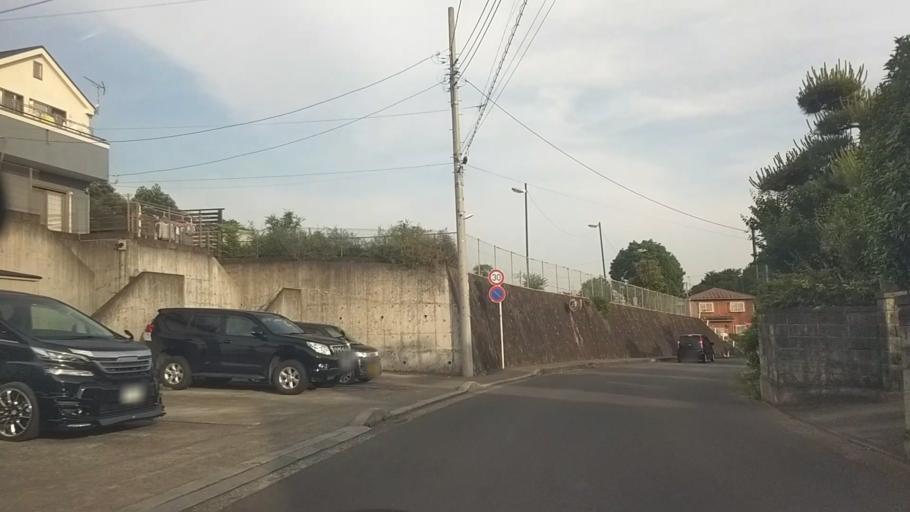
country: JP
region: Kanagawa
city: Odawara
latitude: 35.3195
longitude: 139.1132
